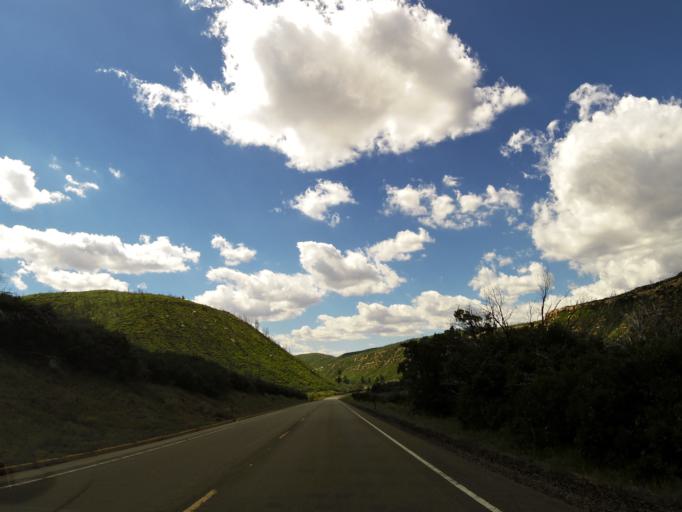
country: US
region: Colorado
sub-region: Montezuma County
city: Mancos
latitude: 37.2904
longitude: -108.4135
